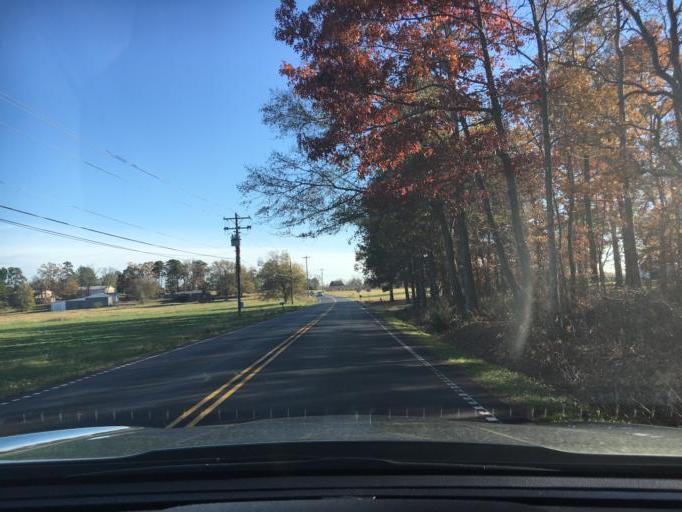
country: US
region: South Carolina
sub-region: Spartanburg County
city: Inman Mills
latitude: 35.0358
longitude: -82.1292
